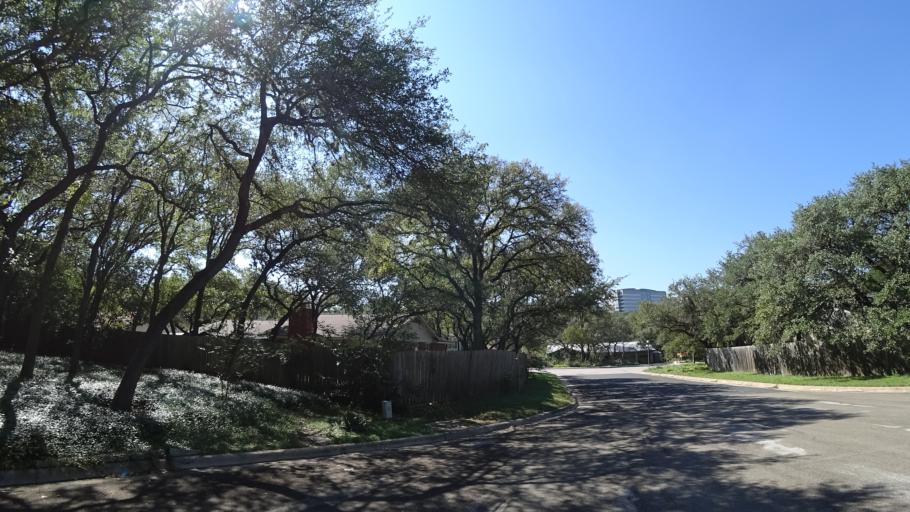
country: US
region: Texas
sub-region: Travis County
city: Rollingwood
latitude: 30.2509
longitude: -97.7947
